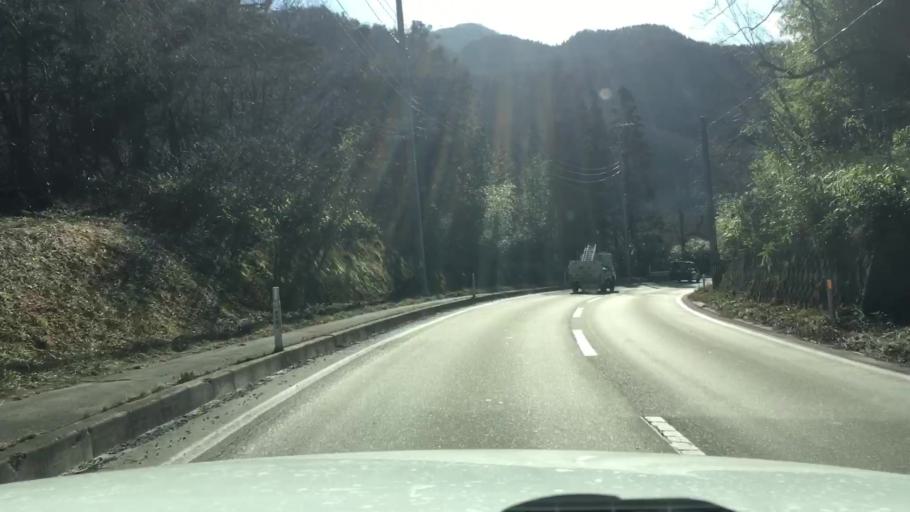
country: JP
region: Iwate
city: Miyako
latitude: 39.6207
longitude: 141.8109
